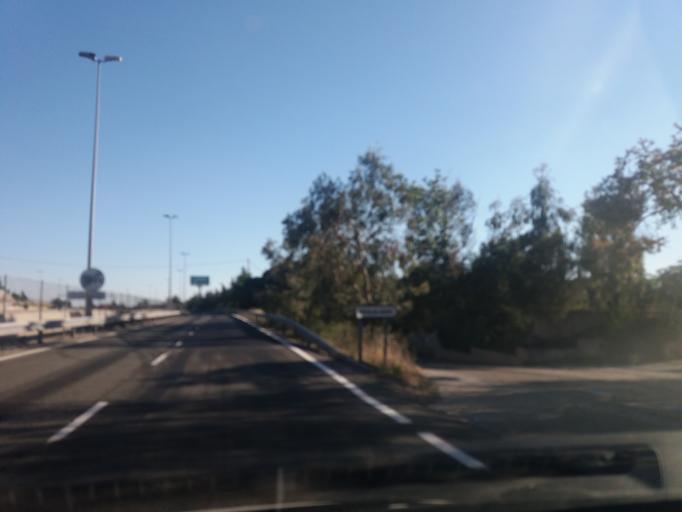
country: ES
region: Madrid
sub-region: Provincia de Madrid
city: Torrelodones
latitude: 40.5920
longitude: -3.9533
